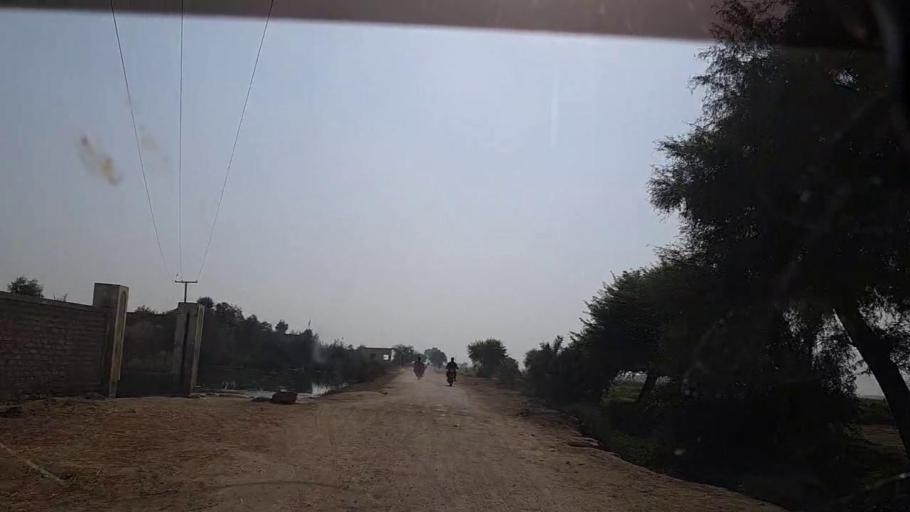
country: PK
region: Sindh
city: Shikarpur
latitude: 28.0984
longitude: 68.6115
